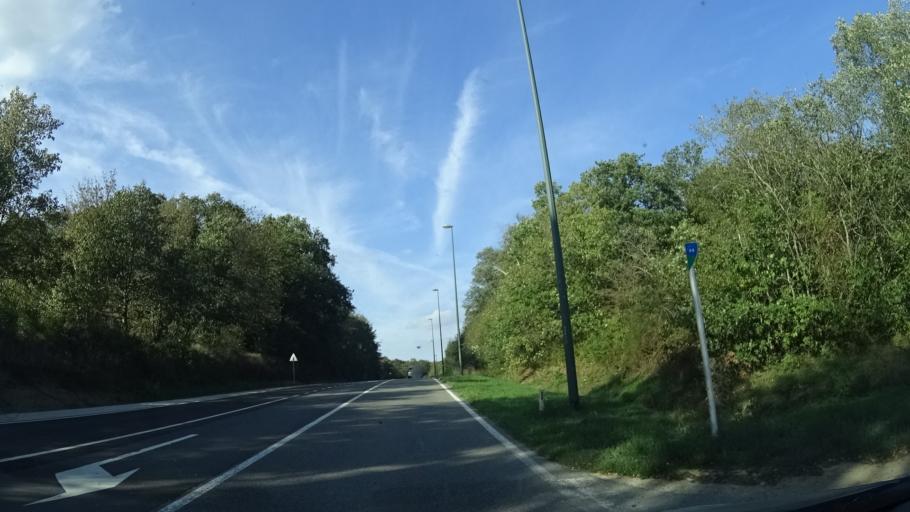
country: BE
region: Wallonia
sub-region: Province de Namur
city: Cerfontaine
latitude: 50.2008
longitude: 4.3758
